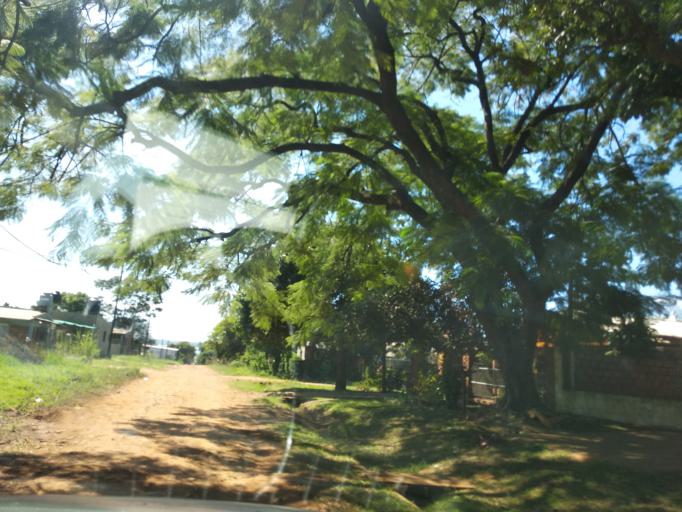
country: AR
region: Misiones
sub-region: Departamento de Capital
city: Posadas
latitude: -27.4280
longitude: -55.8815
